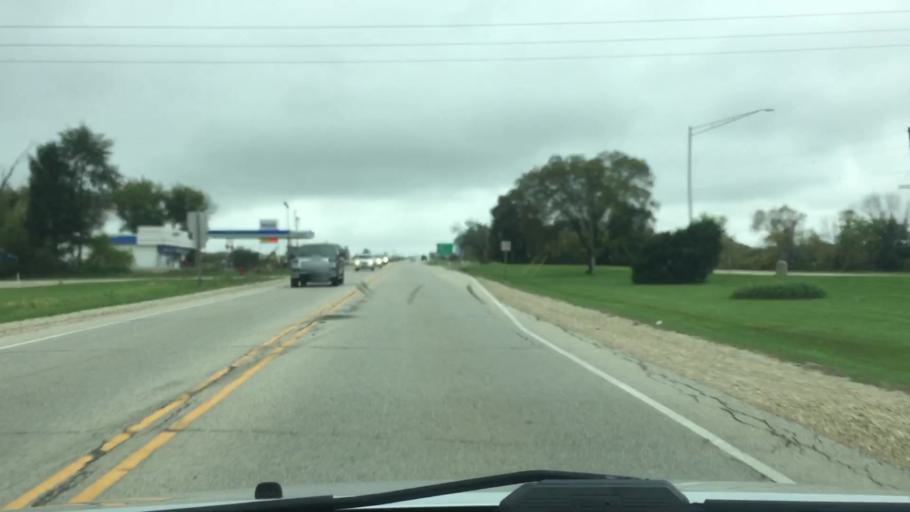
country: US
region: Wisconsin
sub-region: Walworth County
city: Elkhorn
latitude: 42.7033
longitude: -88.5420
